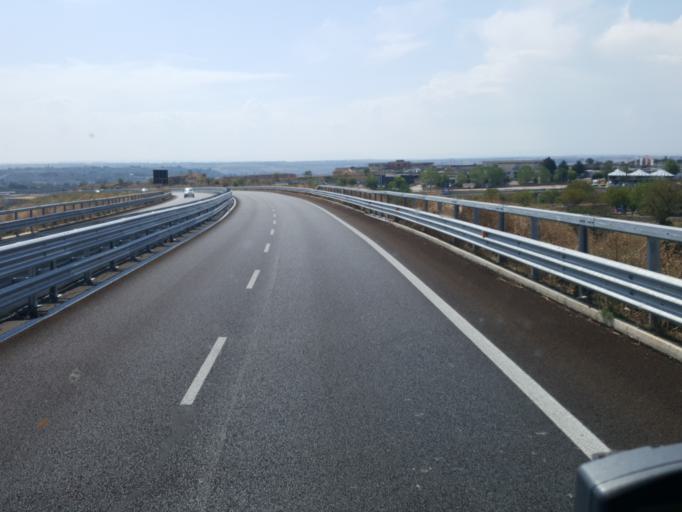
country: IT
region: Apulia
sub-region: Provincia di Bari
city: Altamura
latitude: 40.8132
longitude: 16.5588
